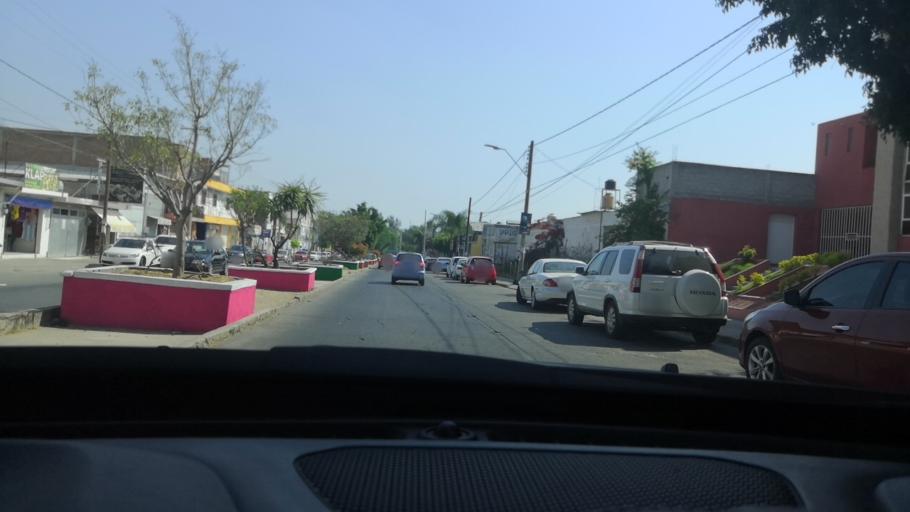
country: MX
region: Guanajuato
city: Leon
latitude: 21.1071
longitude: -101.7026
